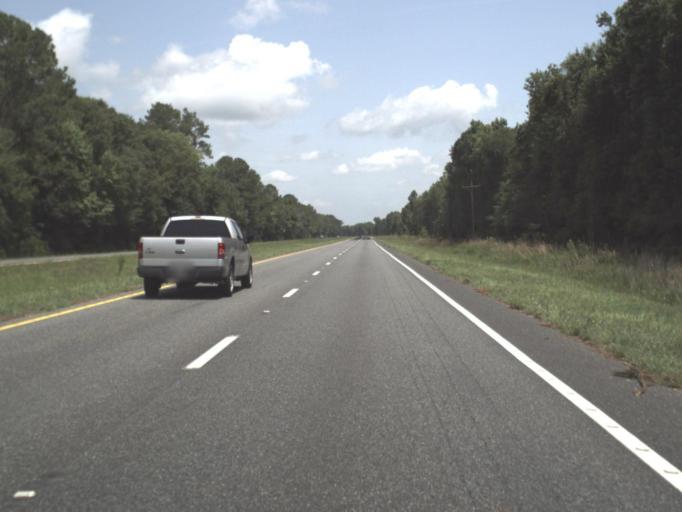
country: US
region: Florida
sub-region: Taylor County
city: Perry
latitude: 29.9338
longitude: -83.4454
